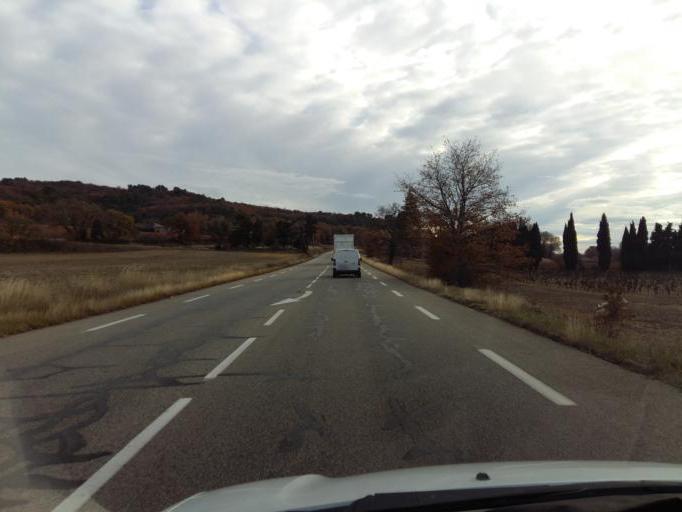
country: FR
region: Provence-Alpes-Cote d'Azur
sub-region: Departement du Vaucluse
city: Visan
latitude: 44.3348
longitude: 4.9472
